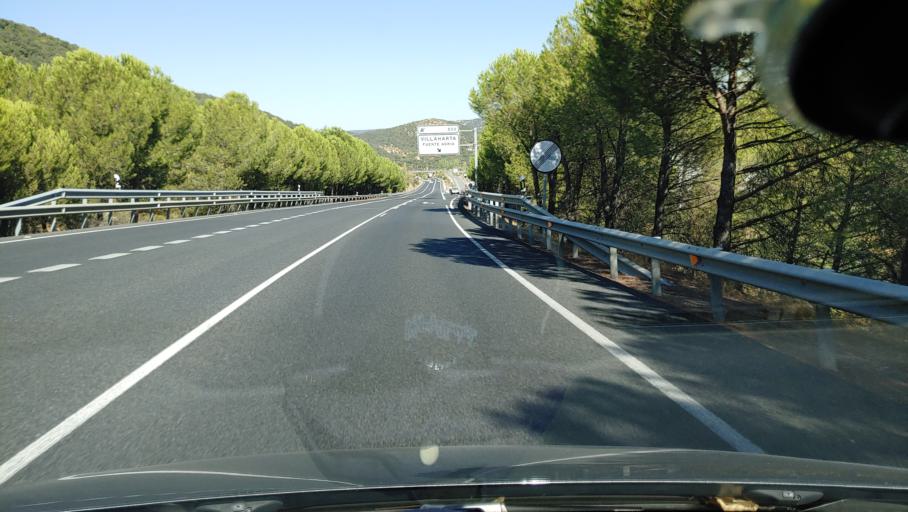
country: ES
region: Andalusia
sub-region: Province of Cordoba
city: Villaharta
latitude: 38.1213
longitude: -4.8961
